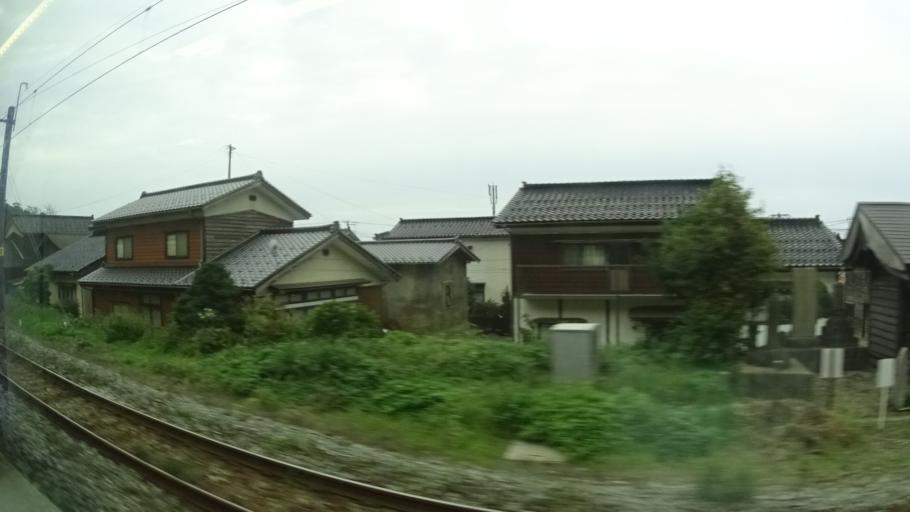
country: JP
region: Yamagata
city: Tsuruoka
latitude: 38.5899
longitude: 139.5656
